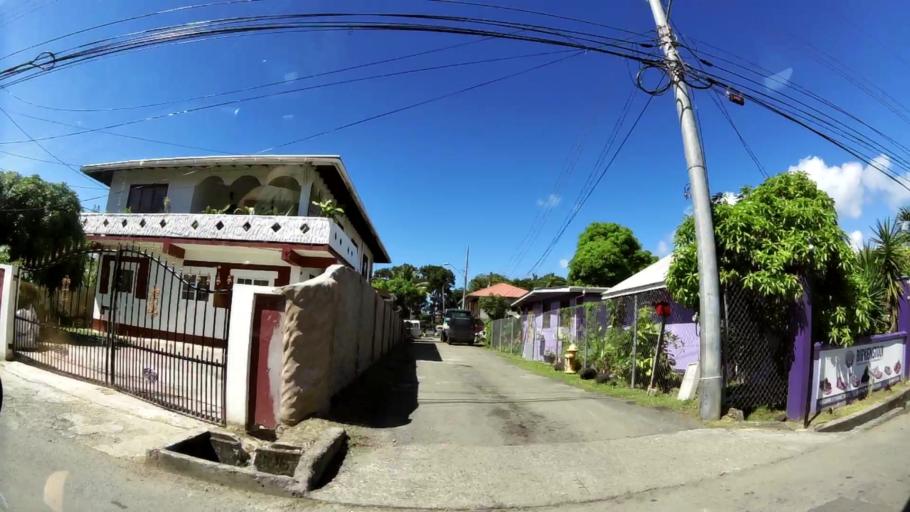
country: TT
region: Tobago
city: Scarborough
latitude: 11.1668
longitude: -60.7815
